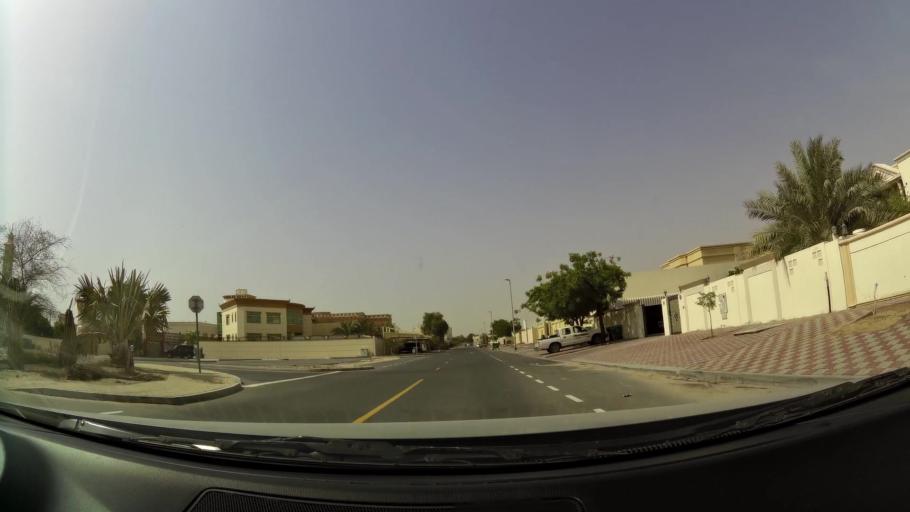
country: AE
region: Ash Shariqah
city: Sharjah
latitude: 25.2485
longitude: 55.4395
